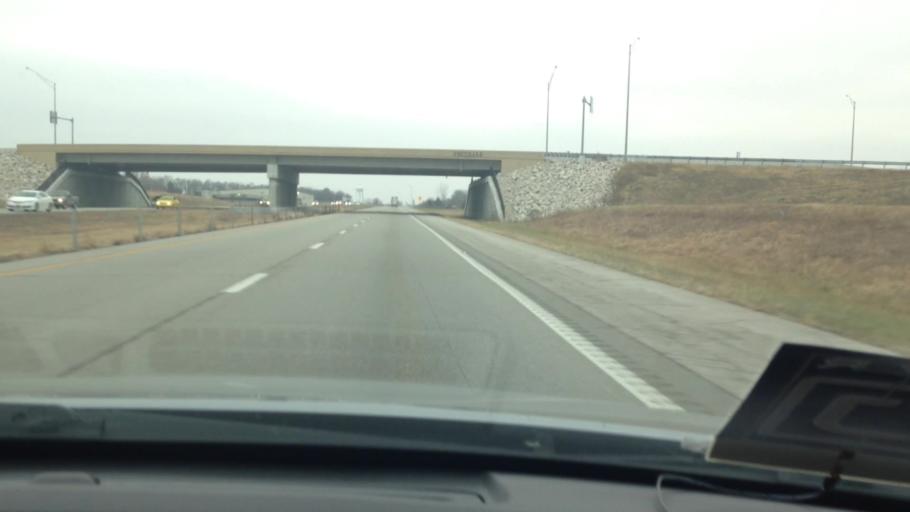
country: US
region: Missouri
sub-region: Cass County
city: Peculiar
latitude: 38.7388
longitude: -94.4696
